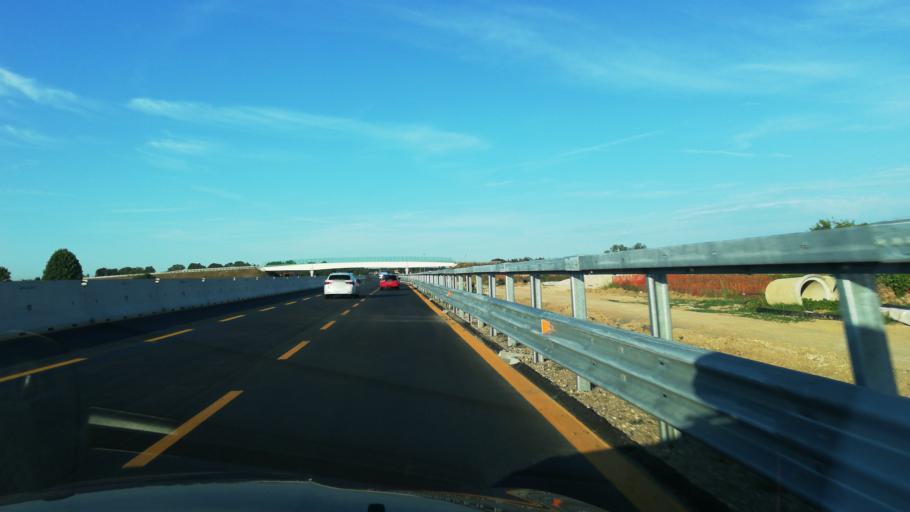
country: IT
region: Friuli Venezia Giulia
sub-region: Provincia di Udine
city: Bagnaria Arsa
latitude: 45.8882
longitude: 13.2707
